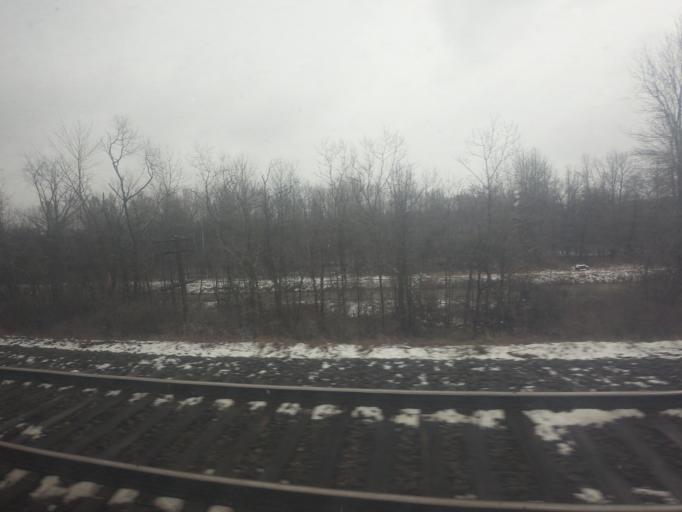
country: CA
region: Ontario
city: Quinte West
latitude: 44.1094
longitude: -77.6037
